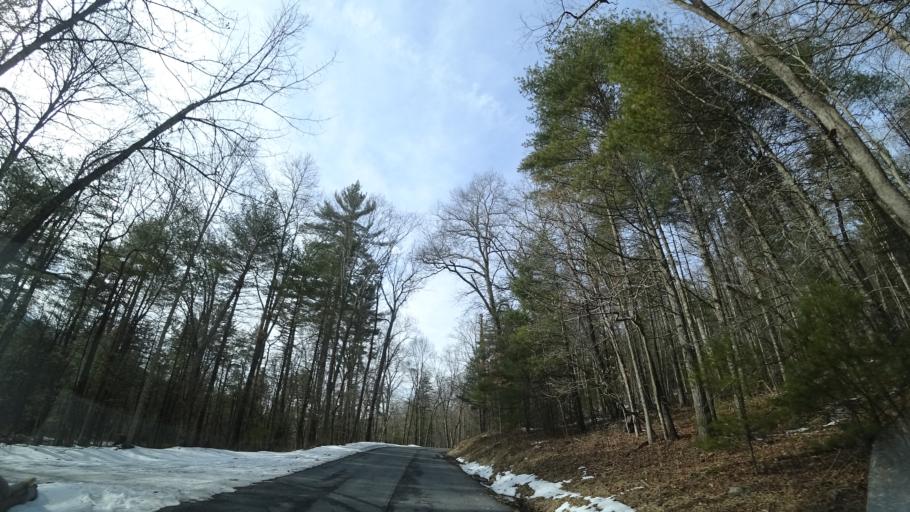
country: US
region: Virginia
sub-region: Shenandoah County
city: Woodstock
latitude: 38.9900
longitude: -78.6575
